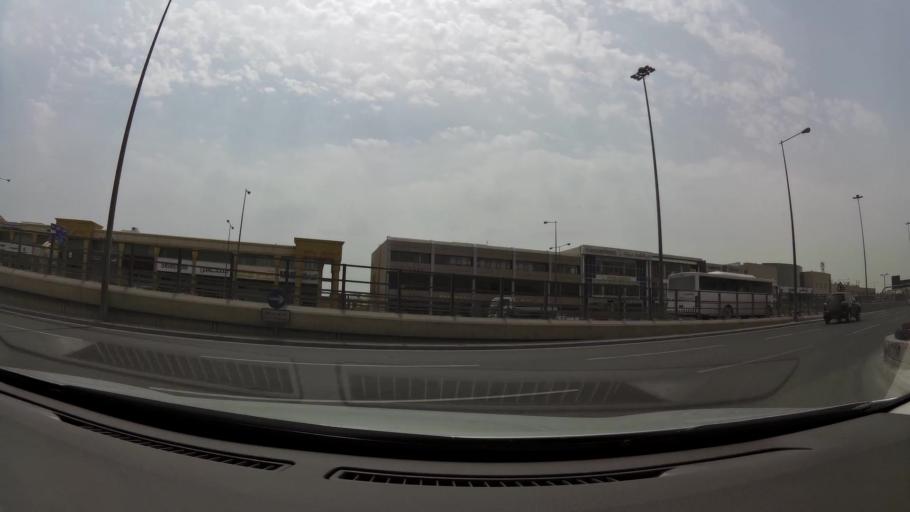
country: QA
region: Baladiyat ad Dawhah
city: Doha
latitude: 25.2628
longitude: 51.4946
